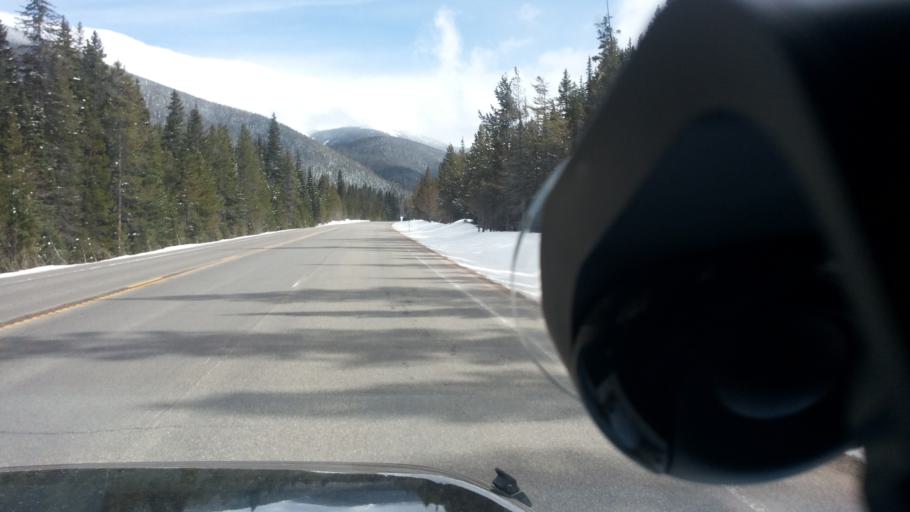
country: US
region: Colorado
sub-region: Grand County
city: Fraser
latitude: 39.8754
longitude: -105.7519
